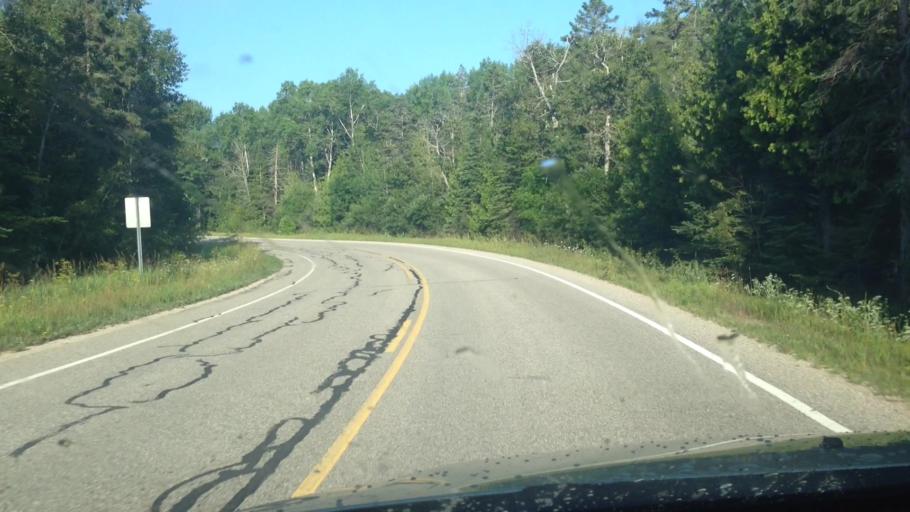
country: US
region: Michigan
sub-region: Mackinac County
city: Saint Ignace
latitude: 45.8931
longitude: -84.7847
